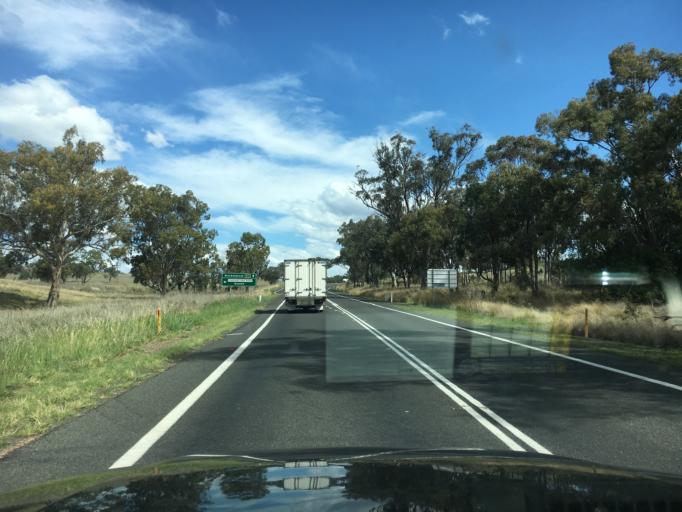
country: AU
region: New South Wales
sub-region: Liverpool Plains
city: Quirindi
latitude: -31.4920
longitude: 150.8643
